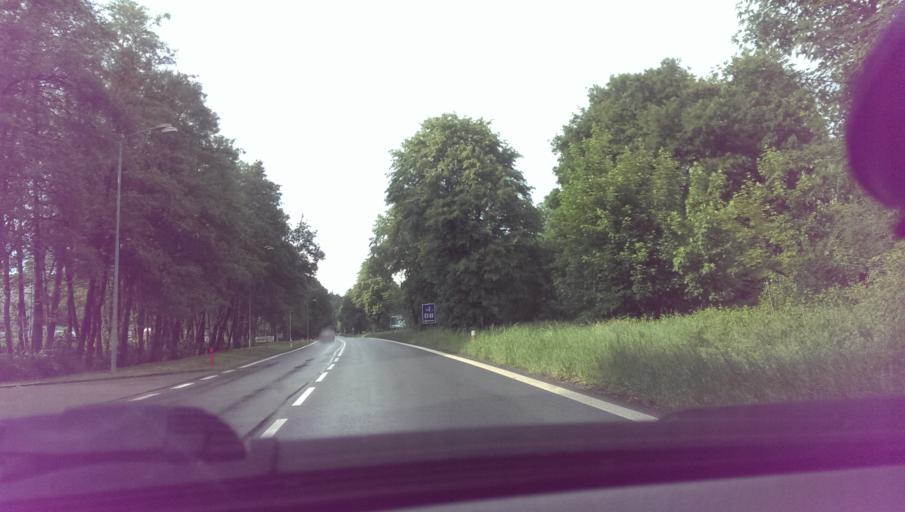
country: CZ
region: Zlin
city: Breznice
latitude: 49.1711
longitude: 17.6405
